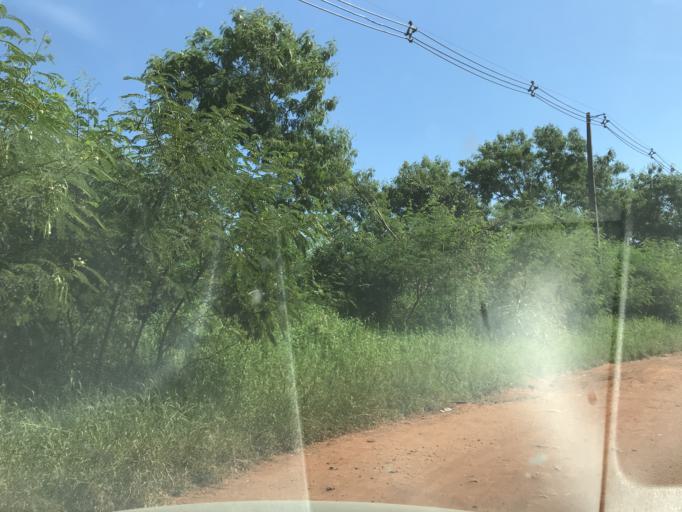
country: BR
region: Parana
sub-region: Palotina
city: Palotina
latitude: -24.2979
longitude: -53.8469
